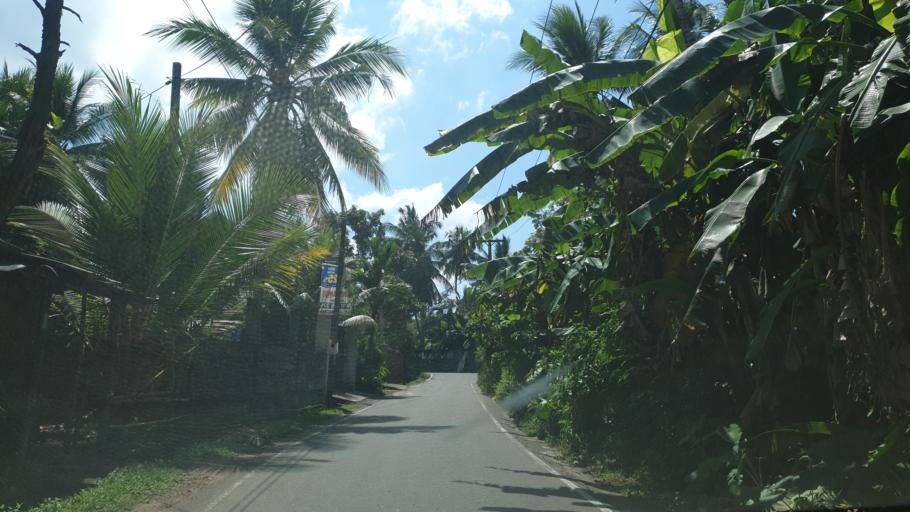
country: LK
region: Western
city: Panadura
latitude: 6.6824
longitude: 79.9291
